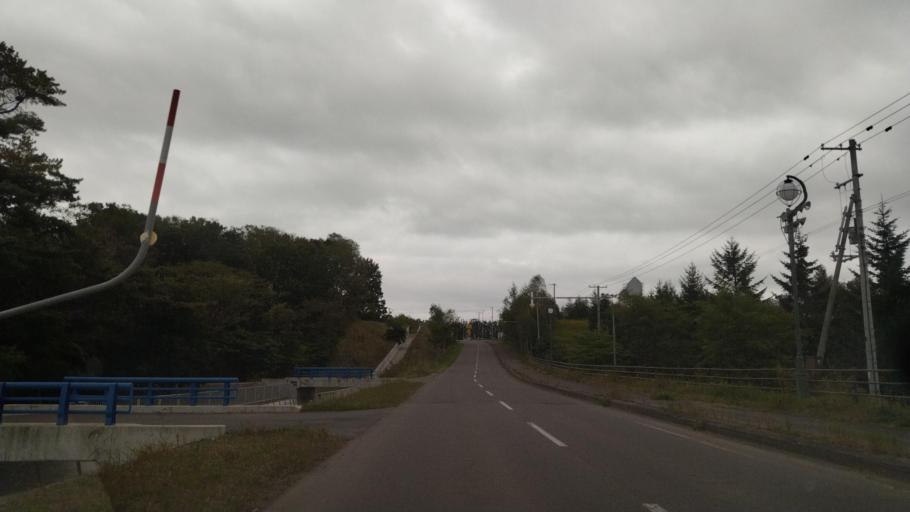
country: JP
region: Hokkaido
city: Otofuke
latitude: 43.2393
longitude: 143.3003
